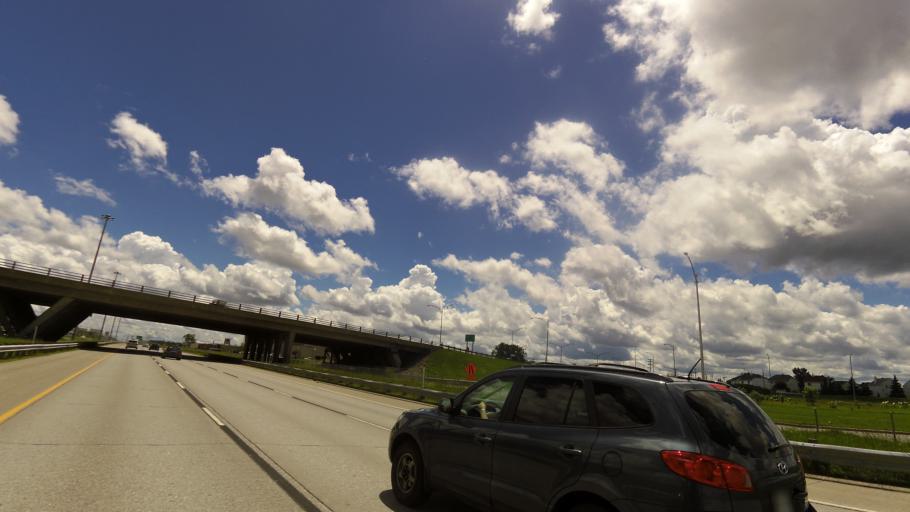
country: CA
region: Quebec
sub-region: Laurentides
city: Boisbriand
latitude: 45.5691
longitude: -73.8250
